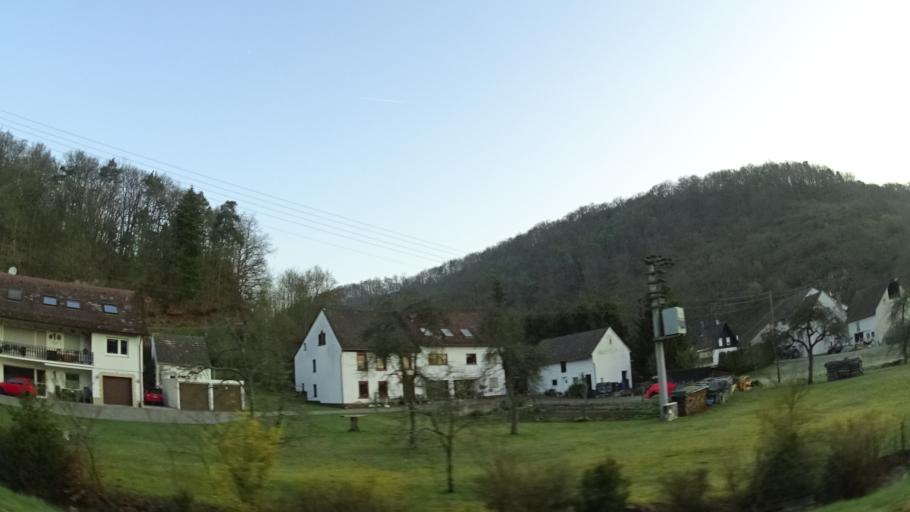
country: DE
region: Rheinland-Pfalz
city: Langweiler
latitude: 49.6682
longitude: 7.5173
